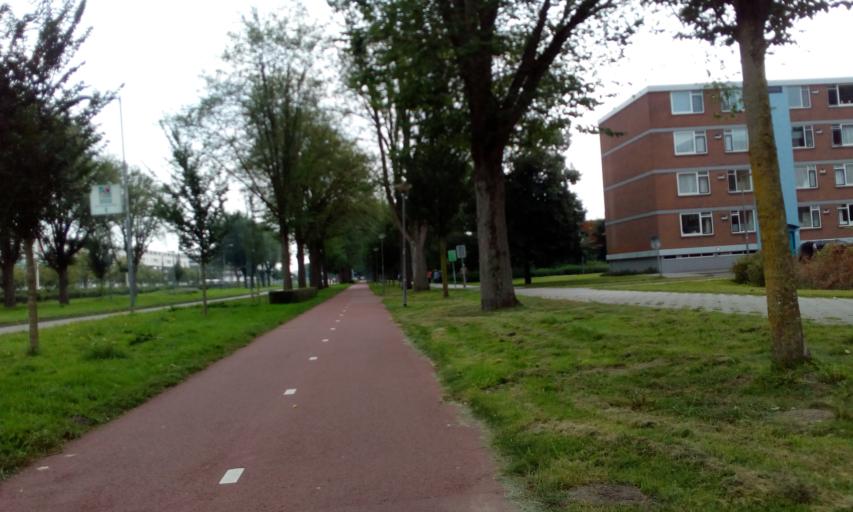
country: NL
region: South Holland
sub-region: Gemeente Rotterdam
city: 's-Gravenland
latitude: 51.9440
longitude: 4.5544
